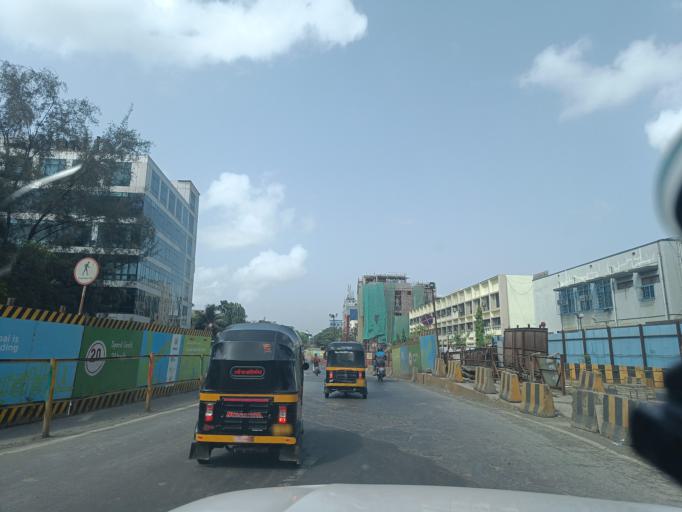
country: IN
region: Maharashtra
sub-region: Mumbai Suburban
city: Powai
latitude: 19.1270
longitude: 72.8743
